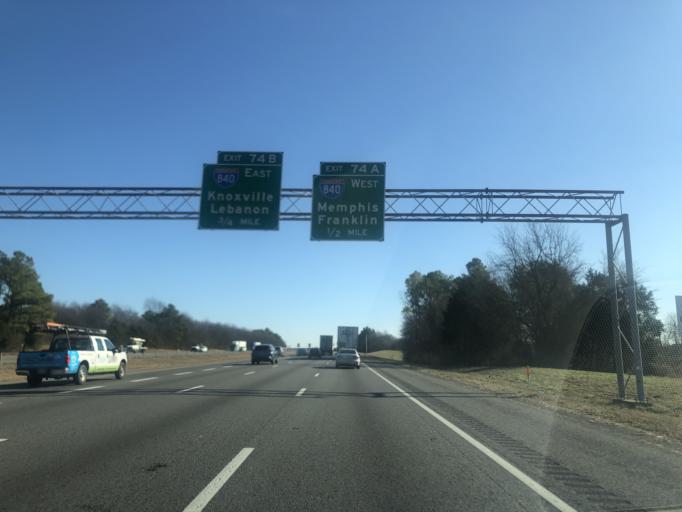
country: US
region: Tennessee
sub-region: Rutherford County
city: Smyrna
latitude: 35.8947
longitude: -86.4878
